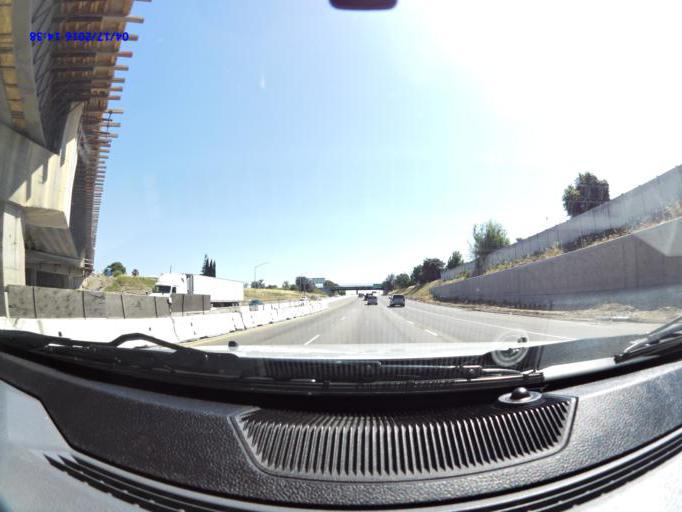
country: US
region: California
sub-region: San Joaquin County
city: Garden Acres
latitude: 37.9438
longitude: -121.2353
